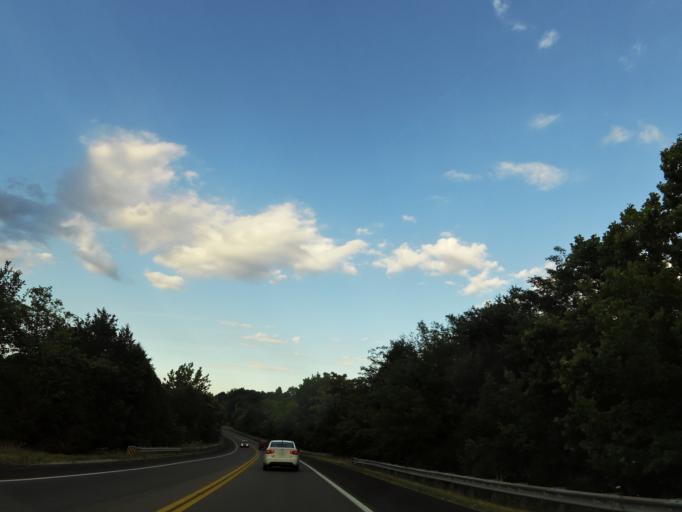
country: US
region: Tennessee
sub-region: Maury County
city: Spring Hill
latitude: 35.6375
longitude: -86.9173
